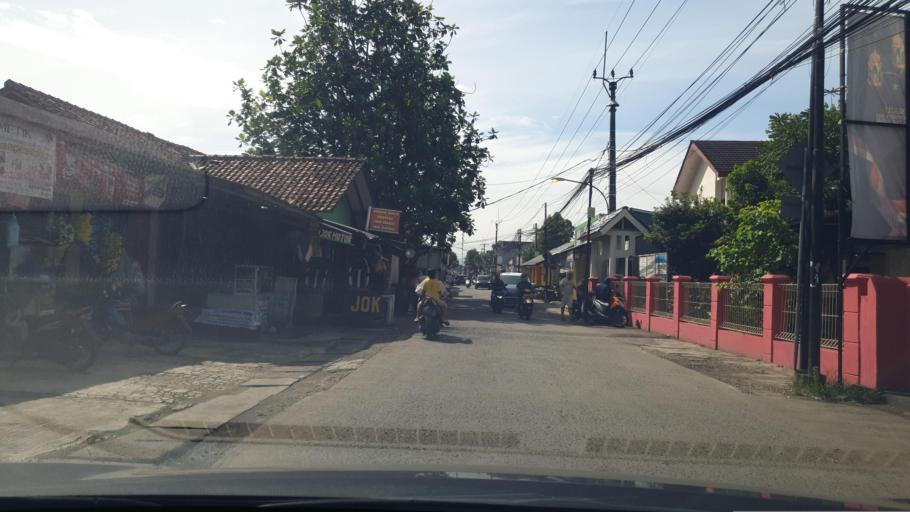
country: ID
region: West Java
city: Sawangan
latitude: -6.4110
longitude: 106.7796
